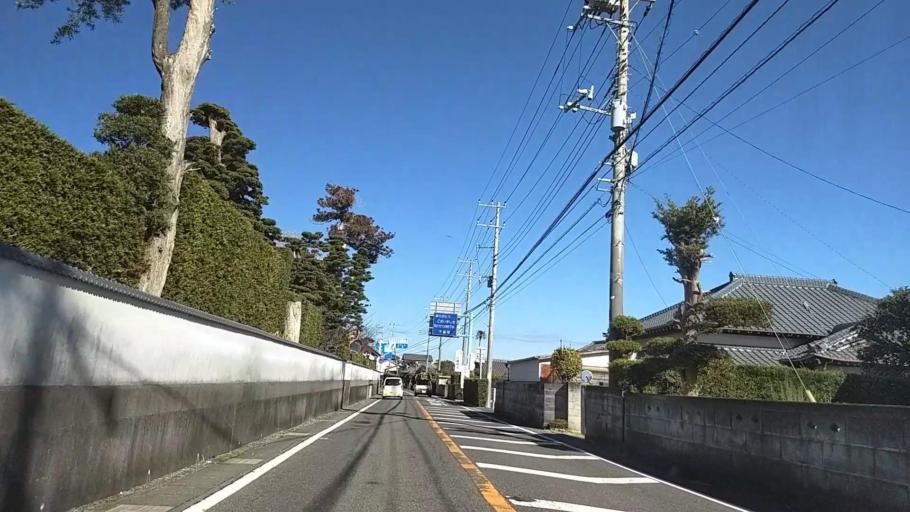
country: JP
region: Chiba
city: Tateyama
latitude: 34.9924
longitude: 139.9674
